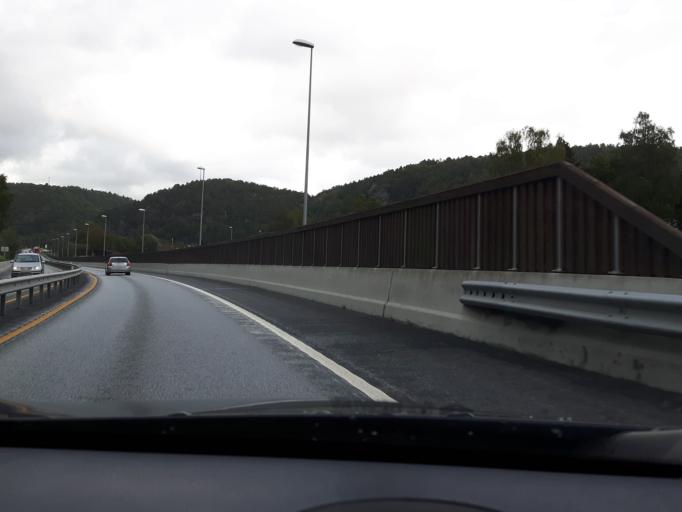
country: NO
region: Vest-Agder
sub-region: Songdalen
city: Nodeland
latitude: 58.1278
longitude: 7.8551
